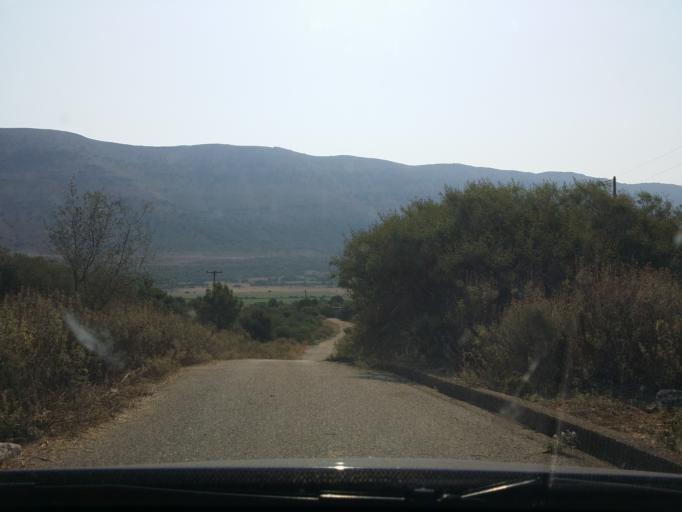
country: GR
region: West Greece
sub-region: Nomos Aitolias kai Akarnanias
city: Stanos
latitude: 38.8256
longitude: 21.1684
